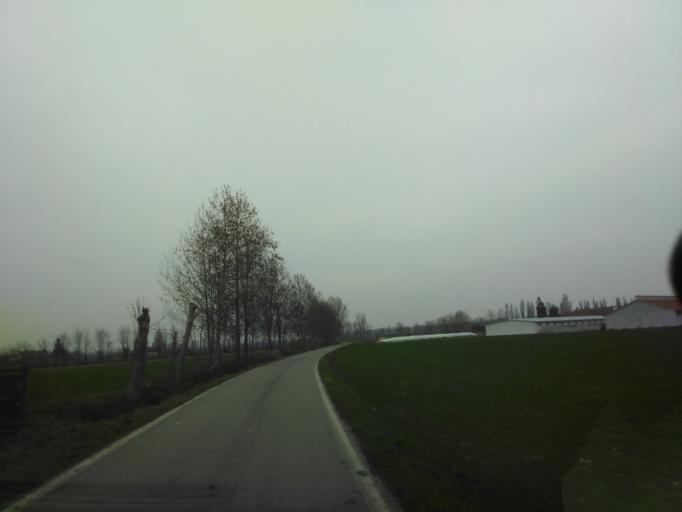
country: IT
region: Lombardy
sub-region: Provincia di Brescia
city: Azzano Mella
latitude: 45.4380
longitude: 10.1460
